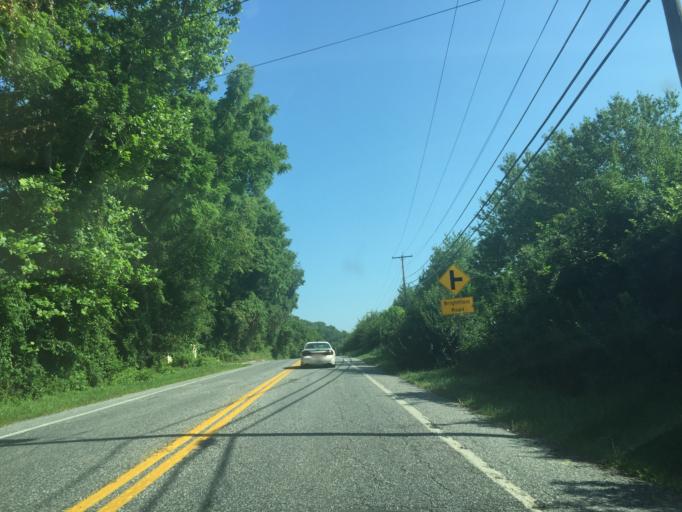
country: US
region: Maryland
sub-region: Baltimore County
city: Mays Chapel
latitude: 39.4038
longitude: -76.6680
